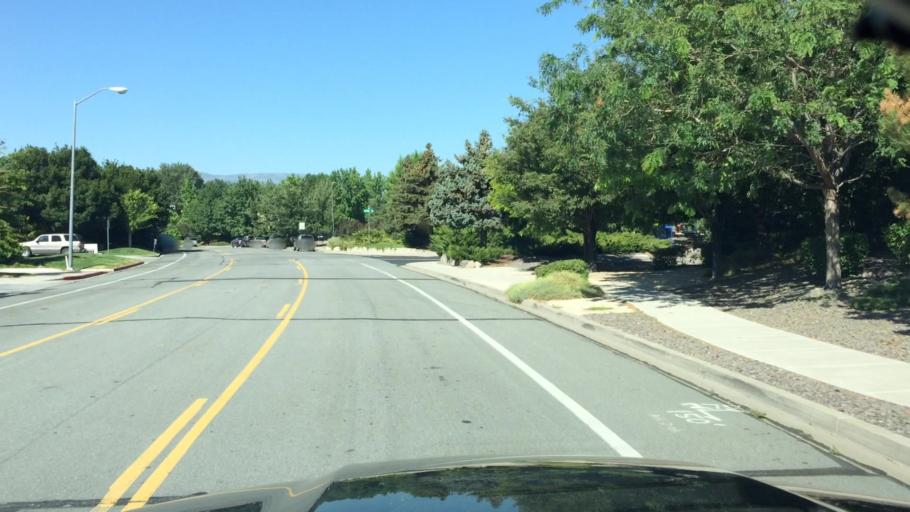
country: US
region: Nevada
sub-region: Washoe County
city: Sparks
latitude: 39.5058
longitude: -119.7509
